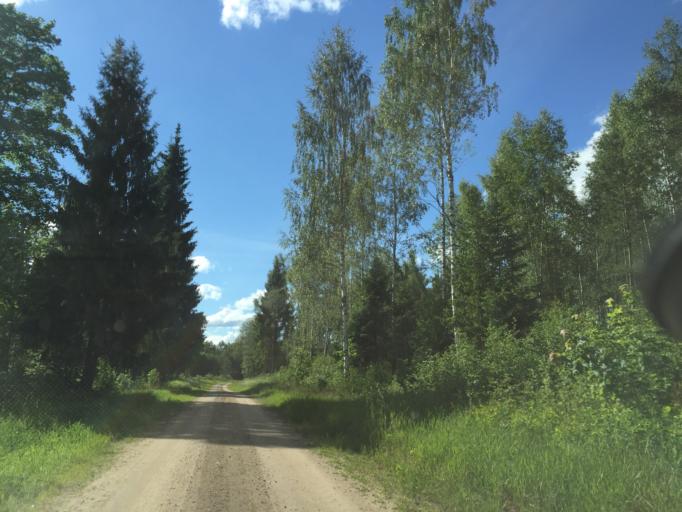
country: LV
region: Vecumnieki
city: Vecumnieki
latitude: 56.4315
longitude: 24.6031
